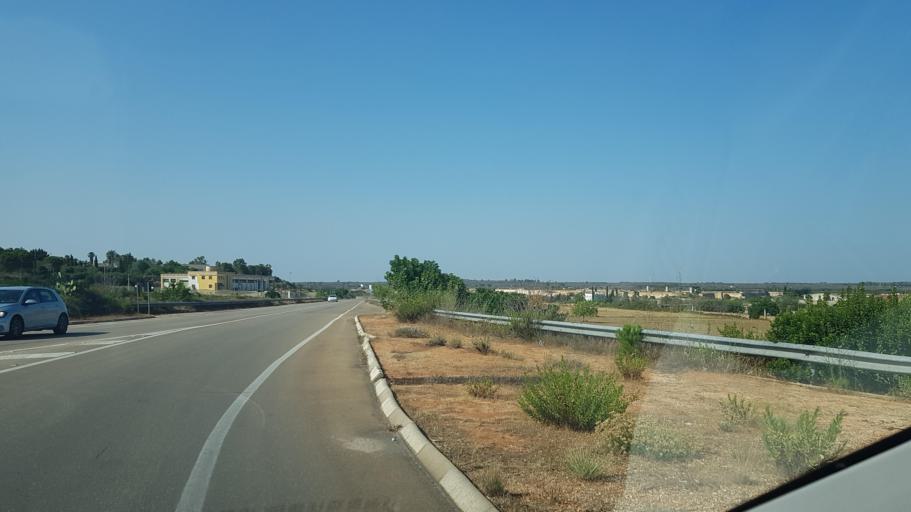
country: IT
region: Apulia
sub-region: Provincia di Lecce
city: Acquarica del Capo
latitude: 39.9188
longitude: 18.2351
